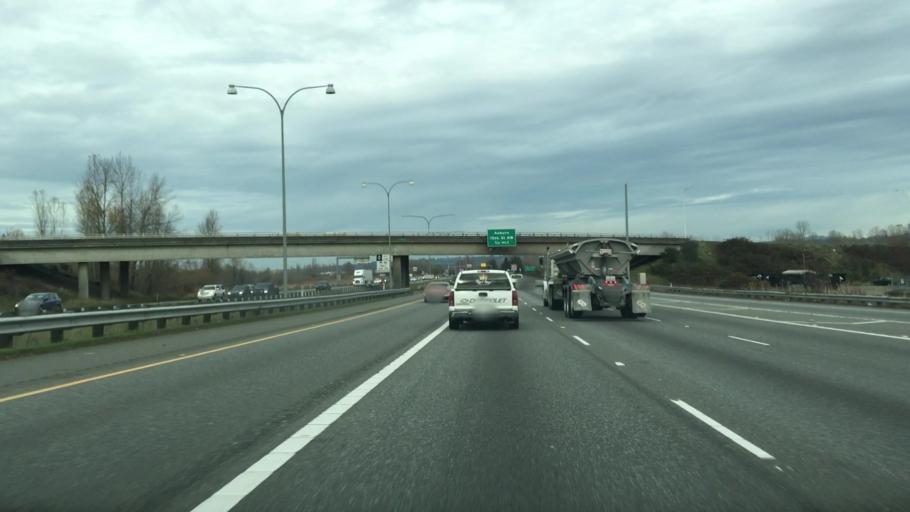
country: US
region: Washington
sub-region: King County
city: Auburn
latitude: 47.3074
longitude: -122.2487
